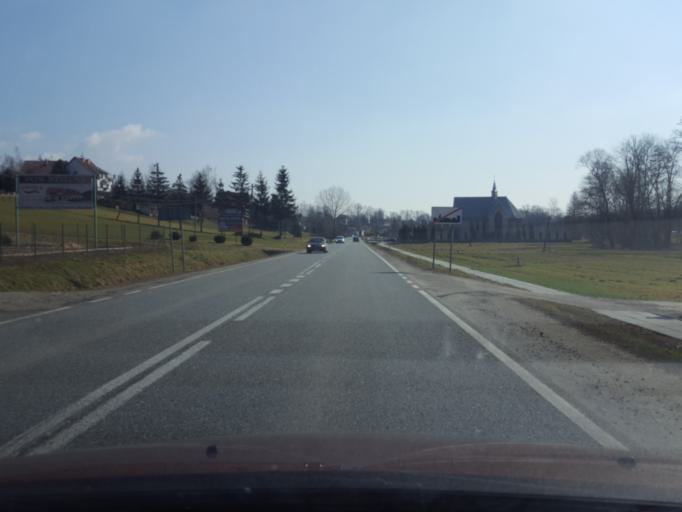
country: PL
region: Lesser Poland Voivodeship
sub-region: Powiat brzeski
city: Czchow
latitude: 49.8531
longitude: 20.6610
